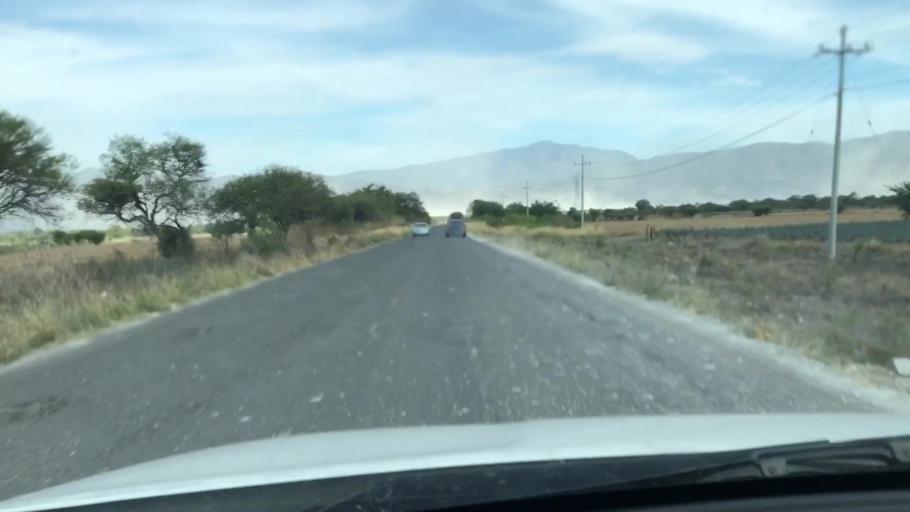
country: MX
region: Jalisco
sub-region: Zacoalco de Torres
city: Barranca de Otates (Barranca de Otatan)
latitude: 20.2844
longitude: -103.6157
